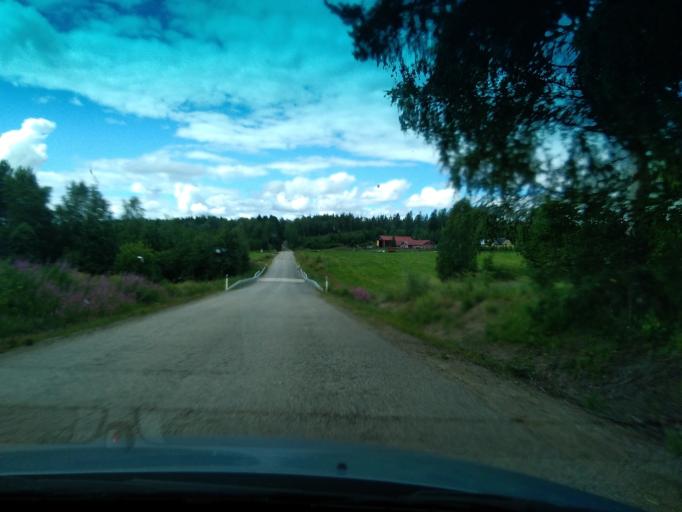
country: FI
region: Central Finland
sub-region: Saarijaervi-Viitasaari
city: Karstula
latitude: 62.8106
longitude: 25.0266
